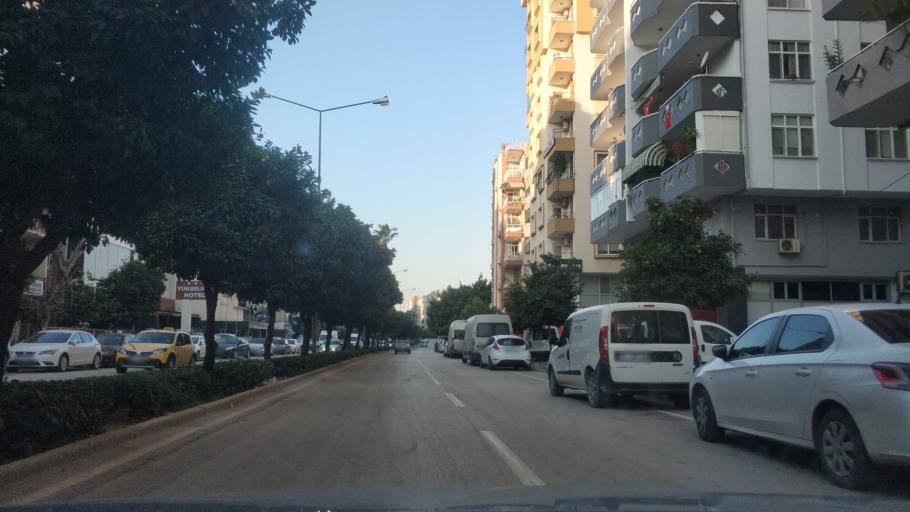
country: TR
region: Adana
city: Adana
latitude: 37.0045
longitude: 35.3287
